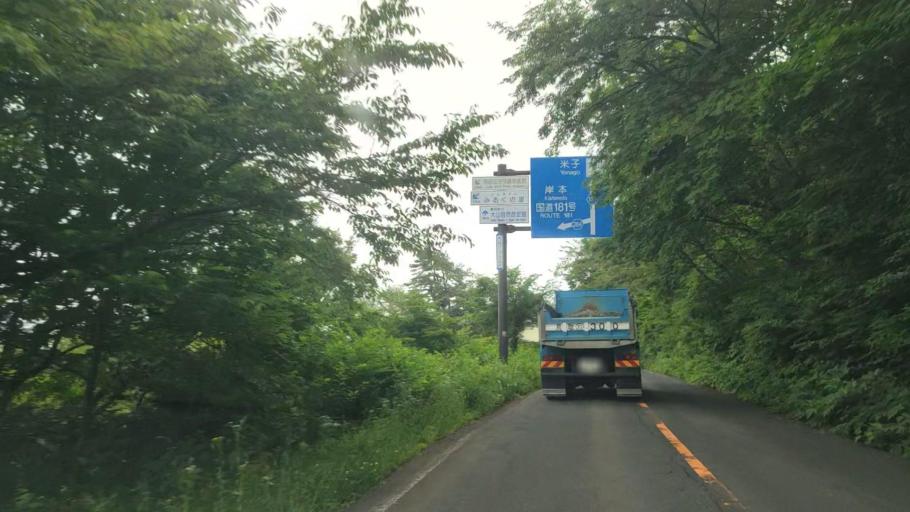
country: JP
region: Tottori
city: Yonago
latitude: 35.3756
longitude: 133.5184
